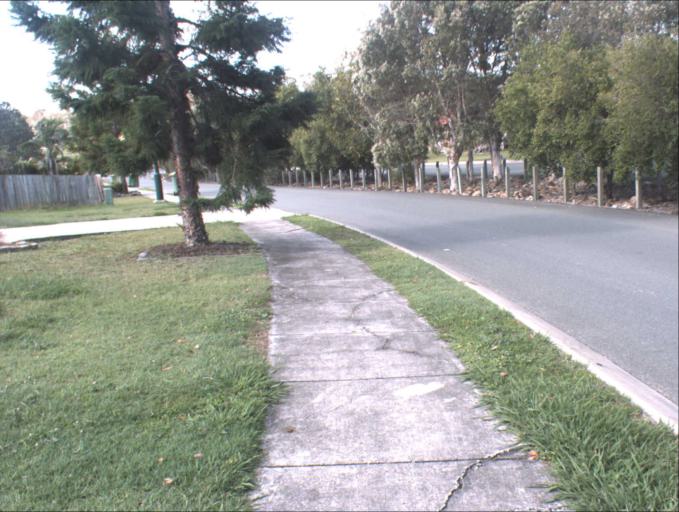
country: AU
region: Queensland
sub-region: Logan
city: Chambers Flat
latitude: -27.7713
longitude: 153.1036
